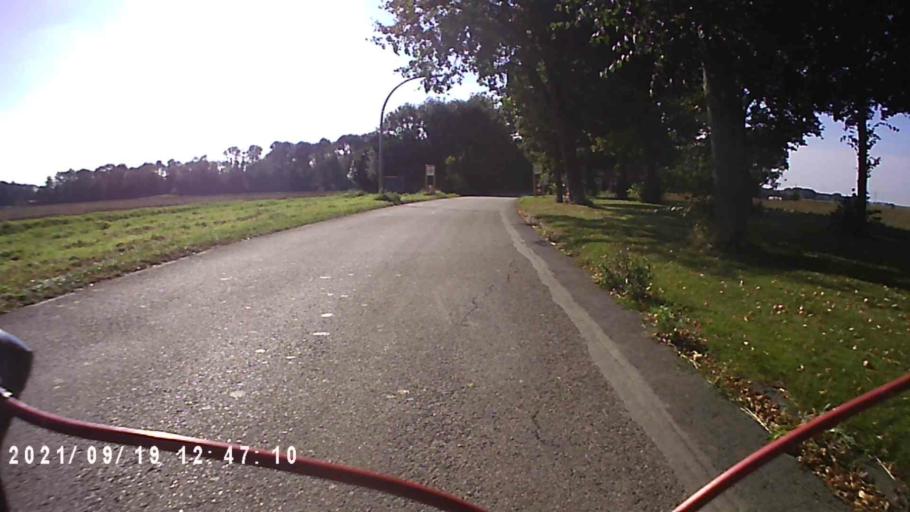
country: NL
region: Groningen
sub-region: Gemeente  Oldambt
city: Winschoten
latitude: 53.2136
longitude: 6.9421
